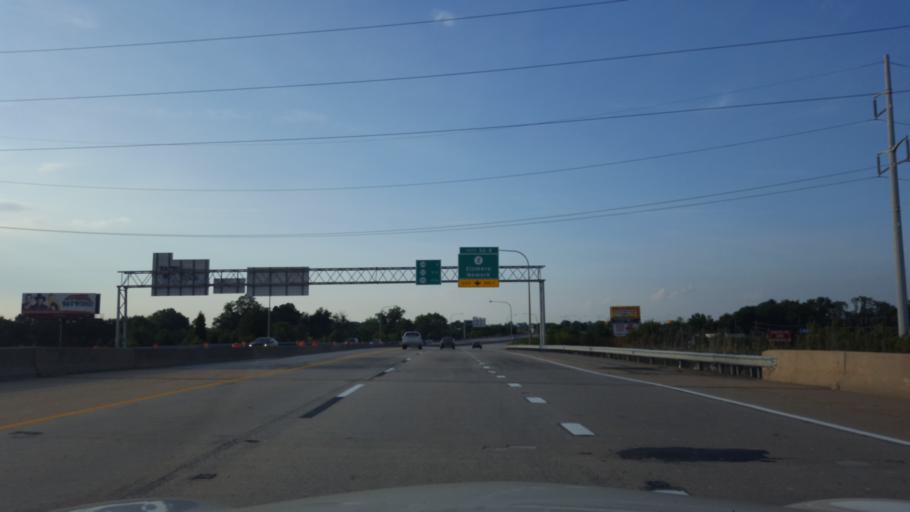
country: US
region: Delaware
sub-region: New Castle County
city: Newport
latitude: 39.7304
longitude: -75.6201
